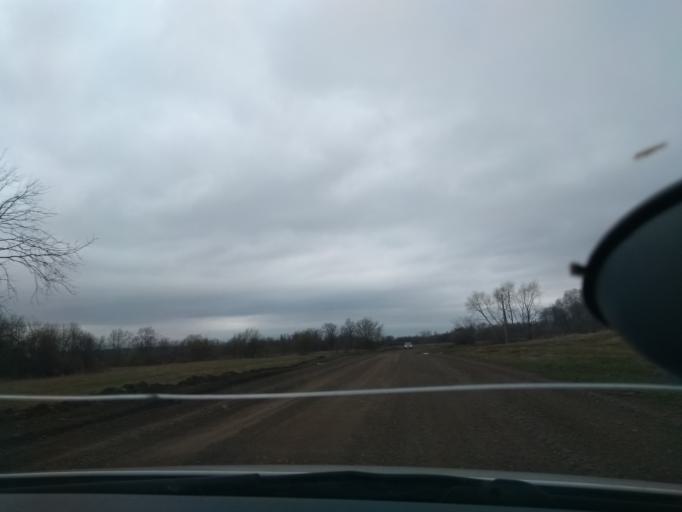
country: RU
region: Perm
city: Orda
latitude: 57.2374
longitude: 56.6111
